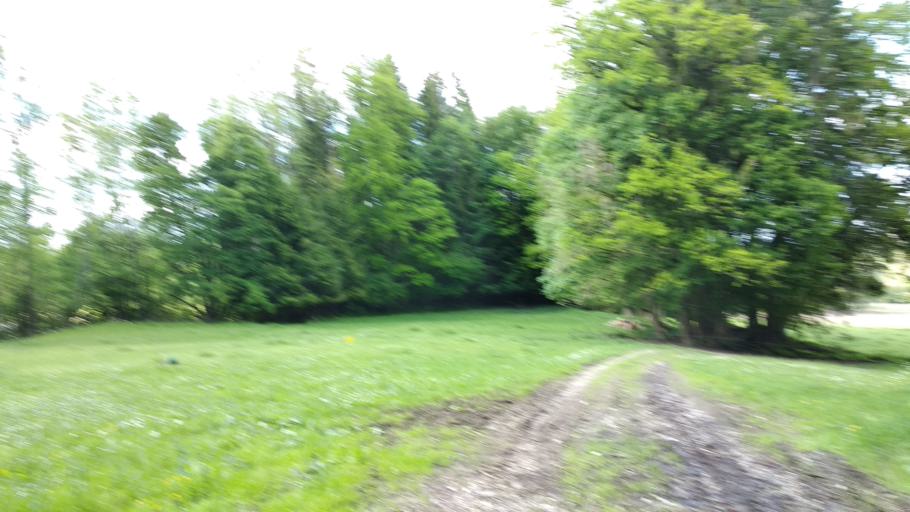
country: DE
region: Bavaria
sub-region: Swabia
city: Kronburg
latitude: 47.8851
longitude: 10.1525
